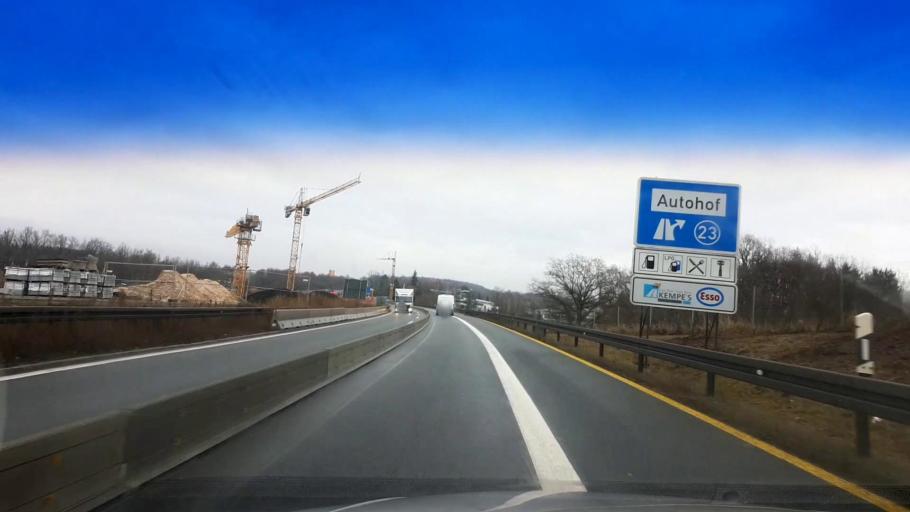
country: DE
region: Bavaria
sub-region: Upper Franconia
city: Thurnau
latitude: 50.0165
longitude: 11.3966
